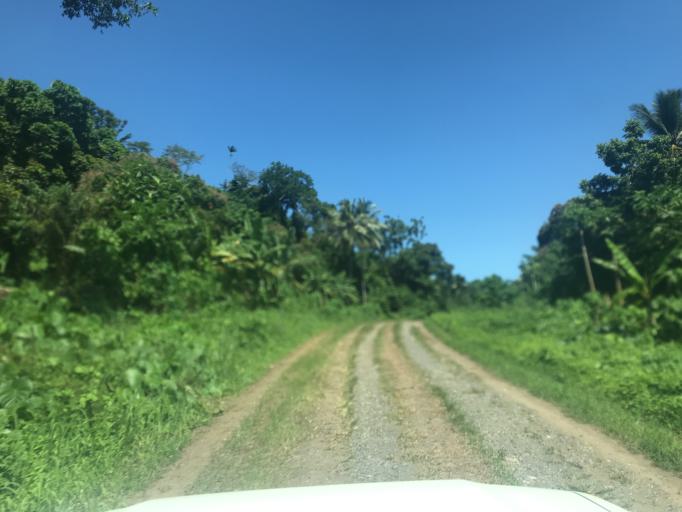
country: VU
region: Sanma
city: Luganville
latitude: -15.6015
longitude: 166.7829
